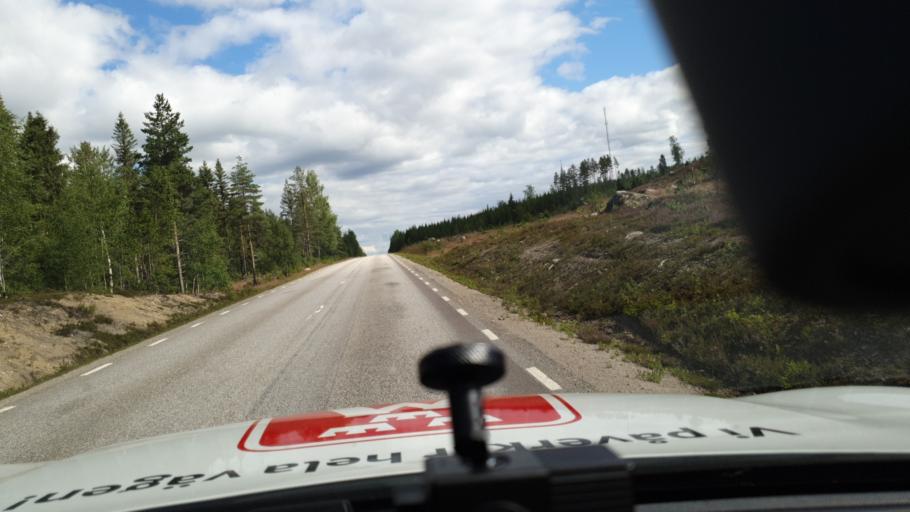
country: NO
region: Hedmark
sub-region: Trysil
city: Innbygda
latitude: 61.0234
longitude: 12.5011
